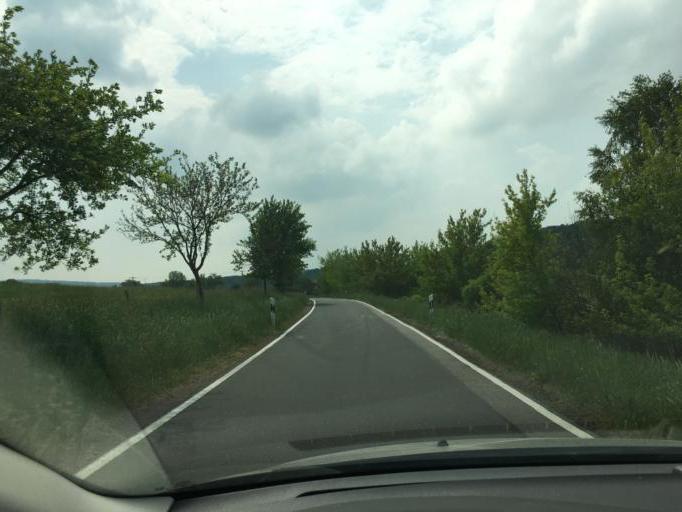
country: DE
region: Saxony
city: Rochlitz
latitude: 51.0751
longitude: 12.7960
